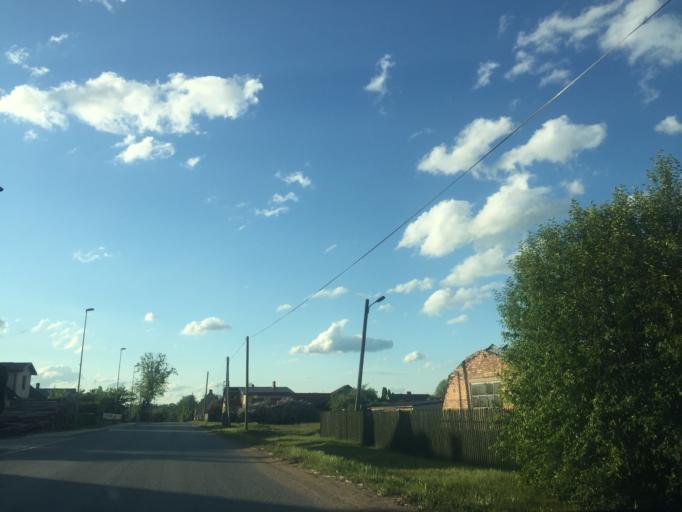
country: LV
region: Kandava
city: Kandava
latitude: 57.0275
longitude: 22.7917
